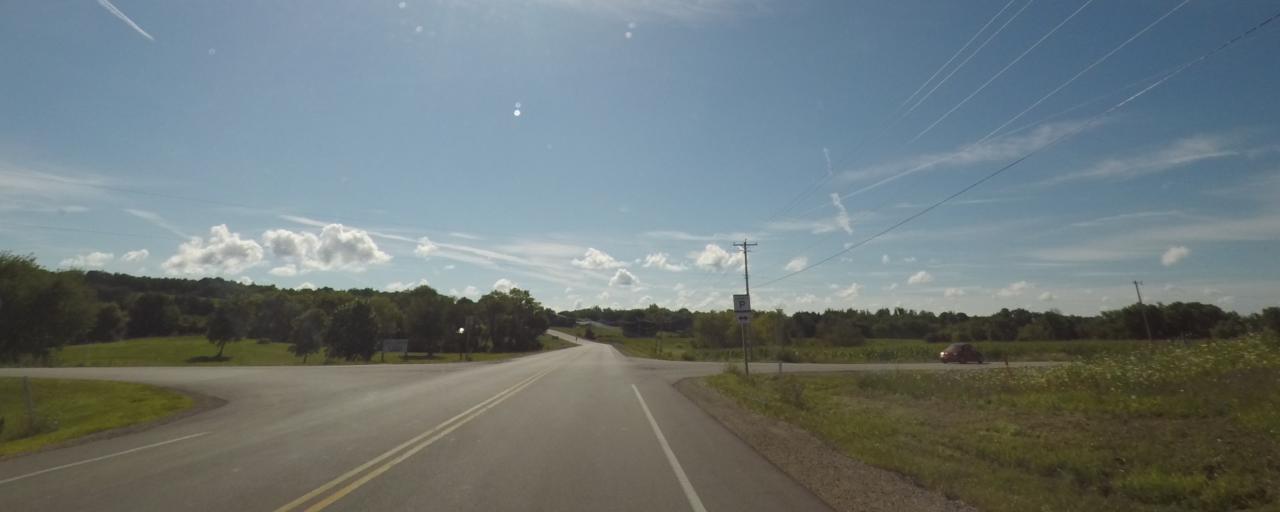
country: US
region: Wisconsin
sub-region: Jefferson County
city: Ixonia
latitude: 43.0752
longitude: -88.6650
